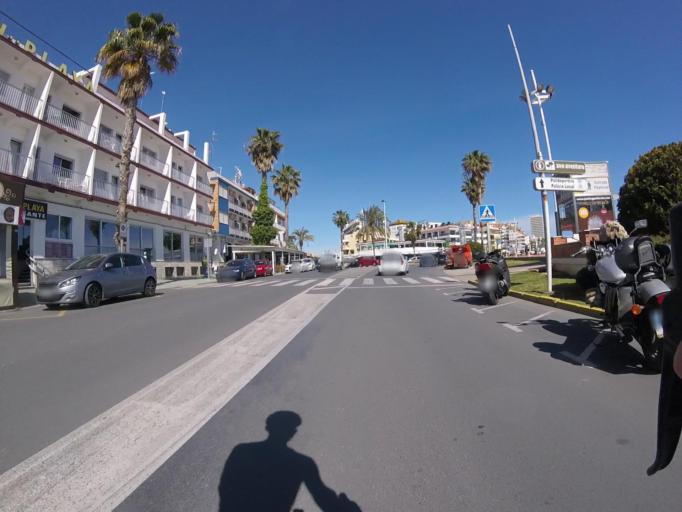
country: ES
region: Valencia
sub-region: Provincia de Castello
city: Peniscola
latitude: 40.3609
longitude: 0.4024
